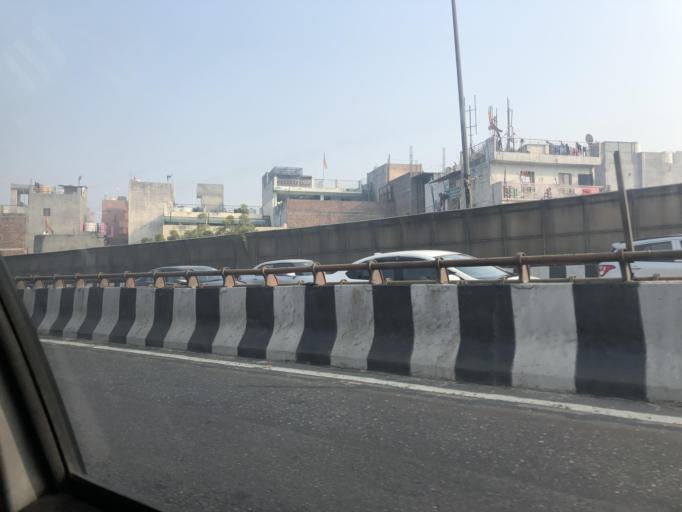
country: IN
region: NCT
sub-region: Central Delhi
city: Karol Bagh
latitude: 28.6206
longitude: 77.1364
